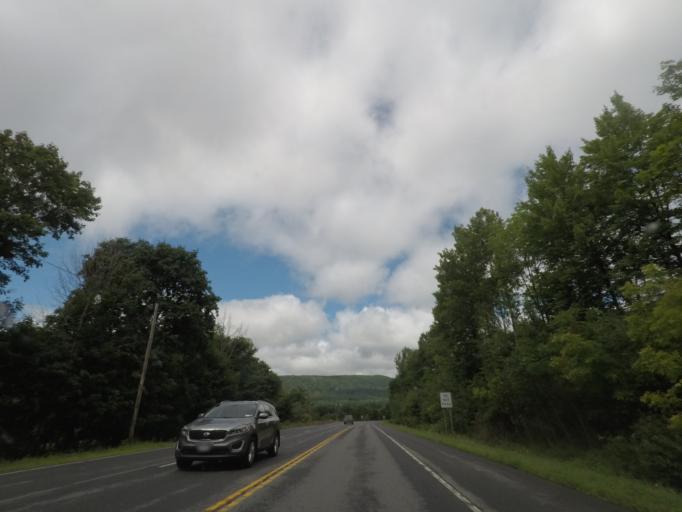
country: US
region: Massachusetts
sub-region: Berkshire County
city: Lanesborough
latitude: 42.6060
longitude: -73.3740
